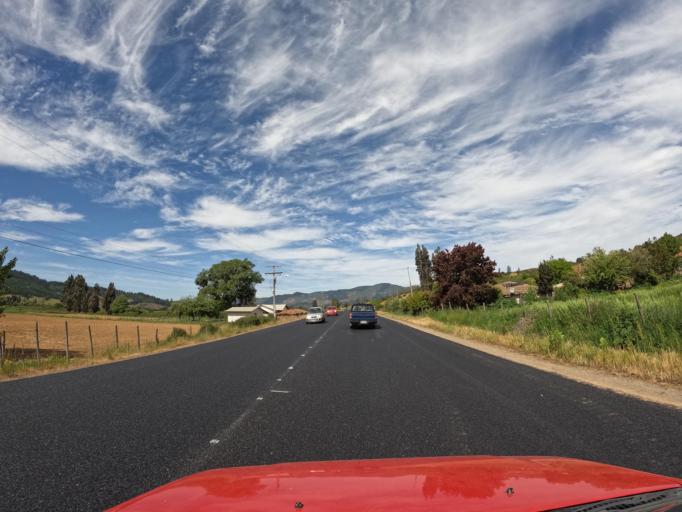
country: CL
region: Maule
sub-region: Provincia de Talca
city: Constitucion
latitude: -35.0994
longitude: -71.9999
